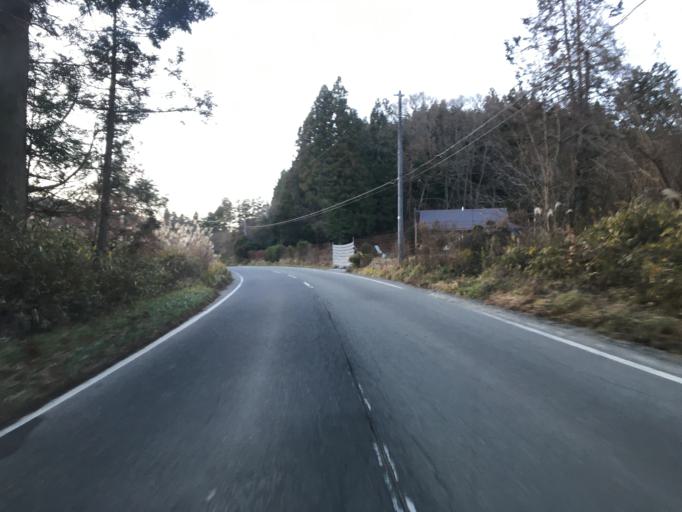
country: JP
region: Fukushima
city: Ishikawa
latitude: 37.2740
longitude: 140.5668
